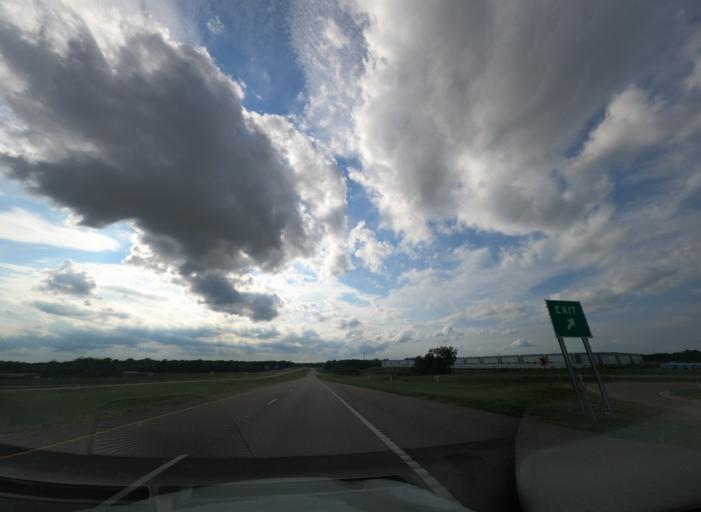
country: US
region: Tennessee
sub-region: Fayette County
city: Piperton
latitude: 34.9865
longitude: -89.5980
